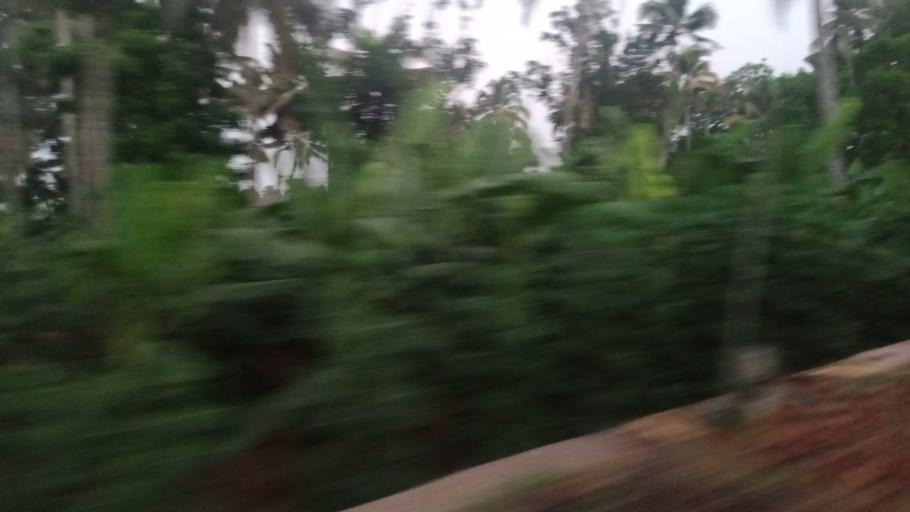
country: IN
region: Kerala
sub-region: Ernakulam
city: Angamali
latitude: 10.1970
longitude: 76.3080
